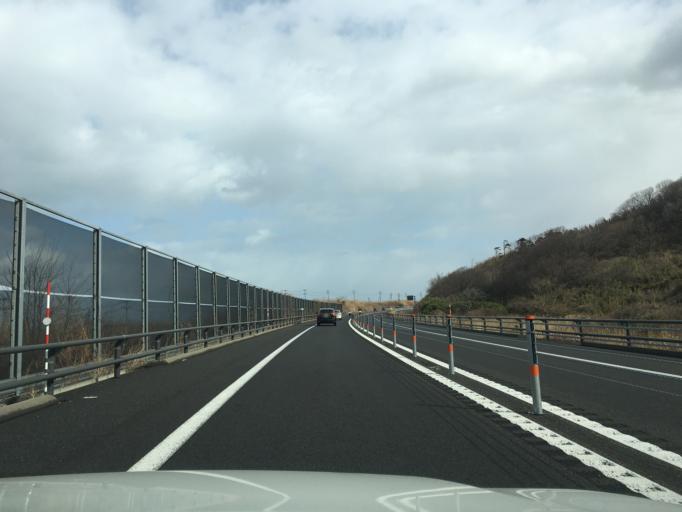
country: JP
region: Yamagata
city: Yuza
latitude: 39.3001
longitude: 139.9771
